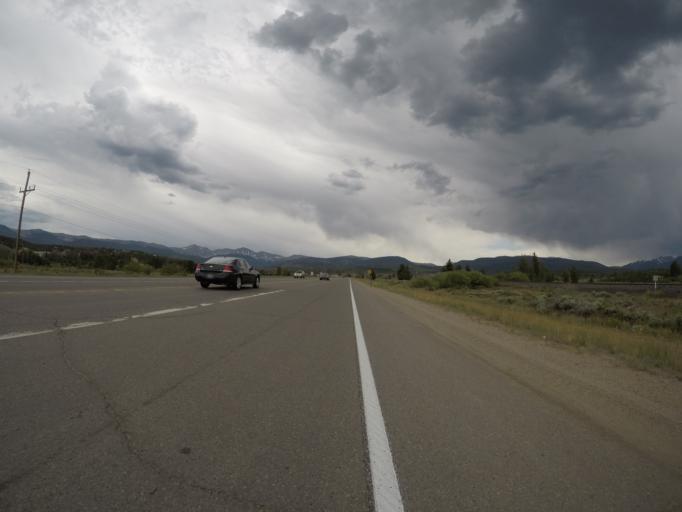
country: US
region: Colorado
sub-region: Grand County
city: Fraser
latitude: 39.9548
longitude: -105.8197
